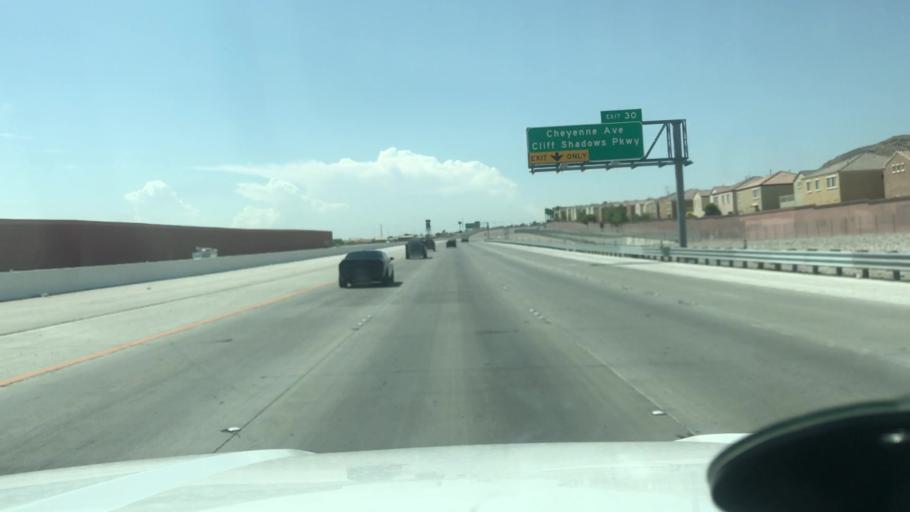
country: US
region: Nevada
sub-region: Clark County
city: Summerlin South
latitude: 36.2294
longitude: -115.3257
